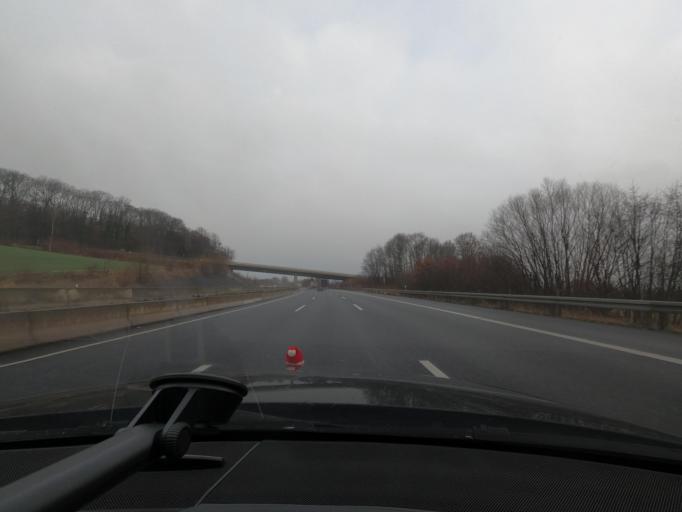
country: DE
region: Lower Saxony
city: Bovenden
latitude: 51.5826
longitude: 9.9126
